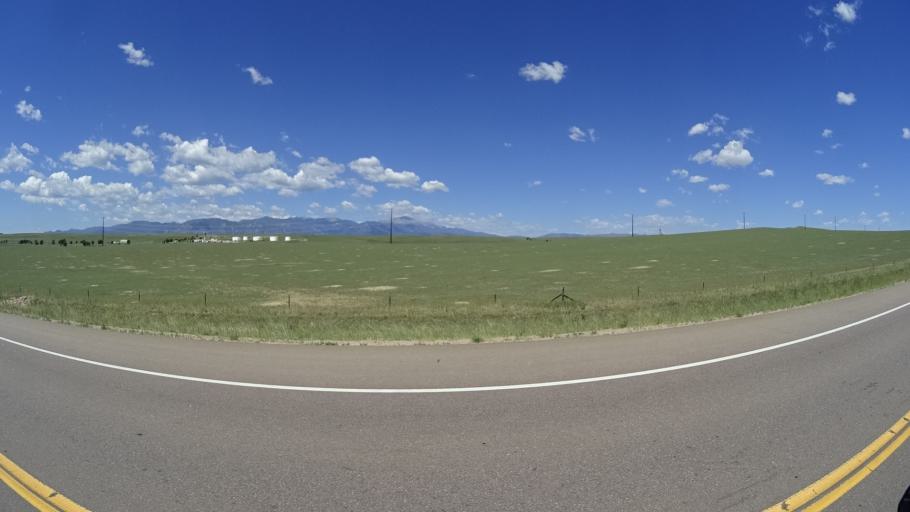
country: US
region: Colorado
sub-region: El Paso County
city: Security-Widefield
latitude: 38.7859
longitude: -104.6591
